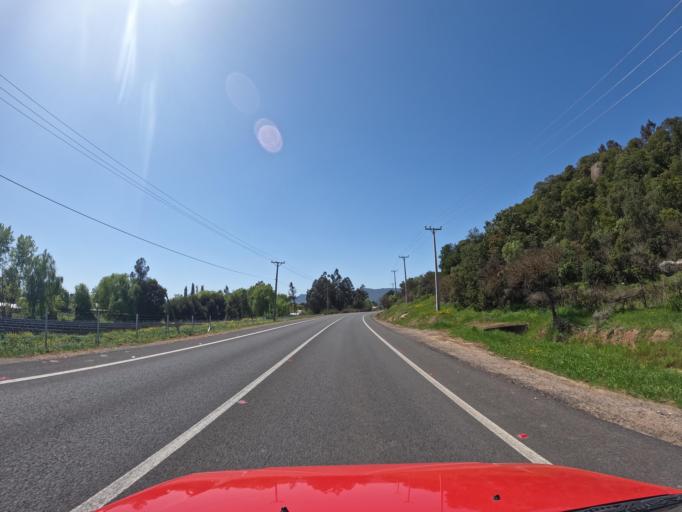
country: CL
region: Maule
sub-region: Provincia de Linares
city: Colbun
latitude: -35.7172
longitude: -71.4079
